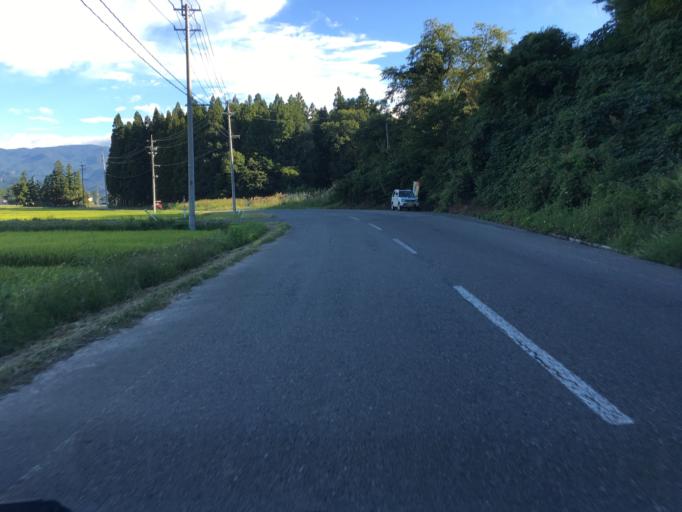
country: JP
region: Yamagata
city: Yonezawa
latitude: 37.8852
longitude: 140.0956
